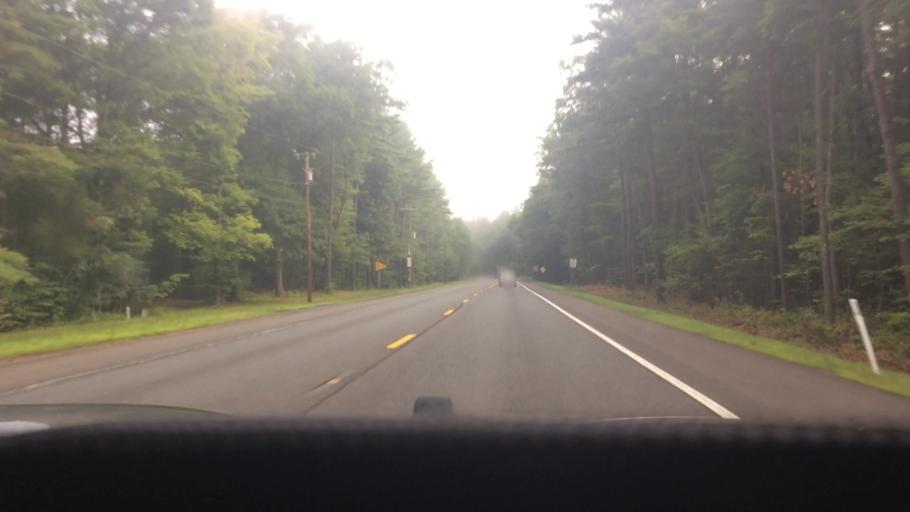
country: US
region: Massachusetts
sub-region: Franklin County
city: Millers Falls
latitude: 42.6034
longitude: -72.5025
